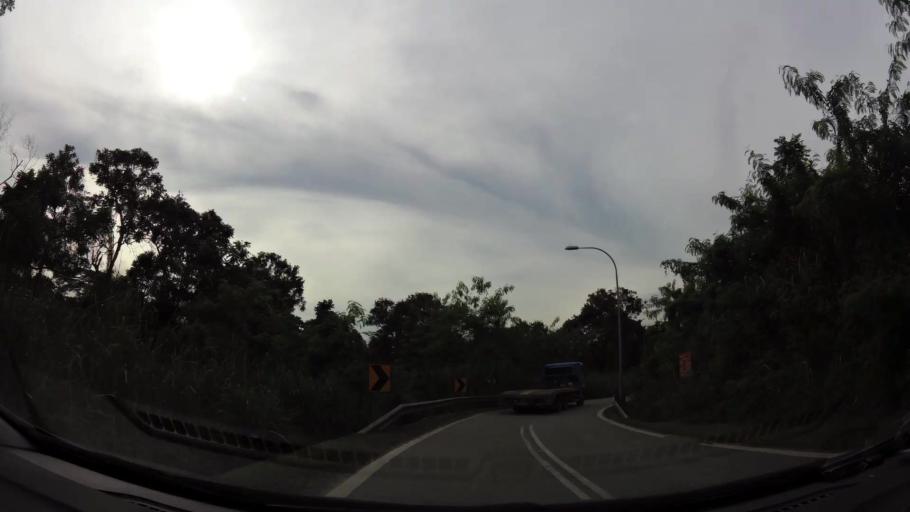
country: MY
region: Johor
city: Johor Bahru
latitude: 1.4164
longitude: 103.7150
